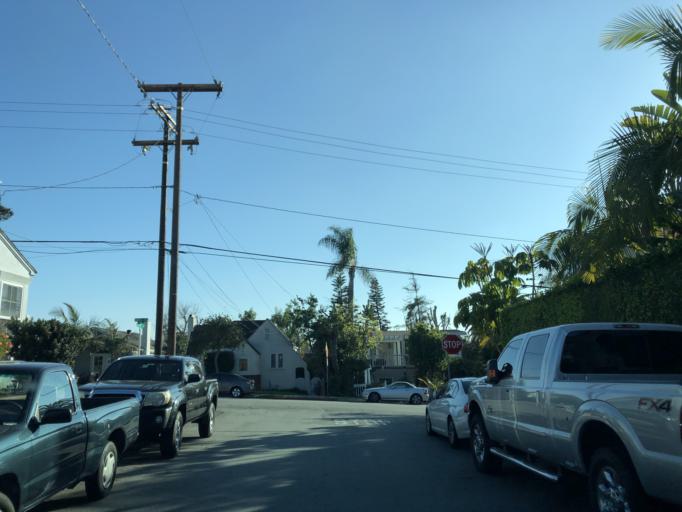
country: US
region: California
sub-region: Los Angeles County
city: El Segundo
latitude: 33.9273
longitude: -118.4150
